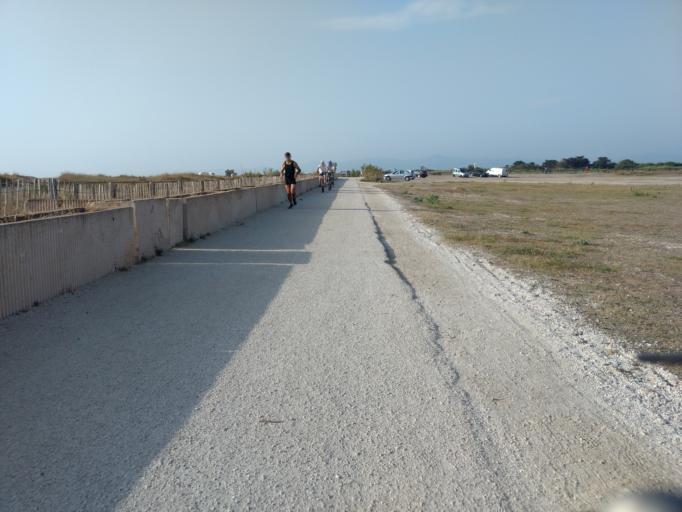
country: FR
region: Languedoc-Roussillon
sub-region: Departement des Pyrenees-Orientales
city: Le Barcares
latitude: 42.7813
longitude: 3.0379
